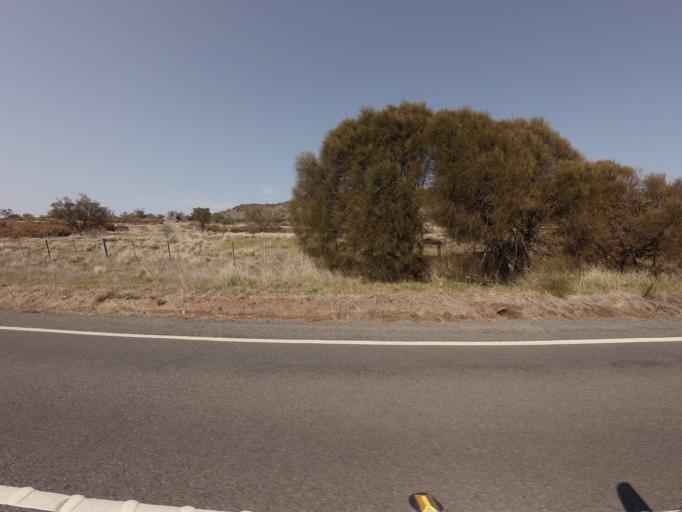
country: AU
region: Tasmania
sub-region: Northern Midlands
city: Evandale
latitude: -41.8148
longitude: 147.5569
